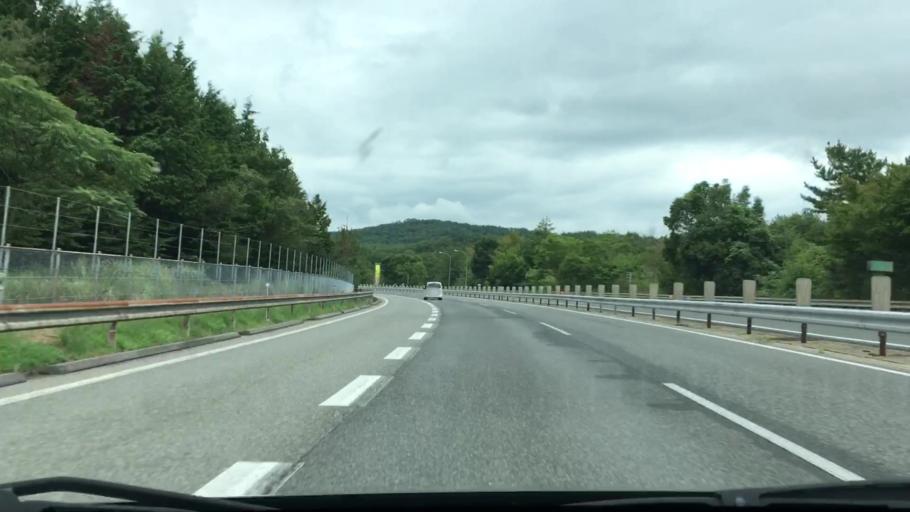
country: JP
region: Hiroshima
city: Miyoshi
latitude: 34.7565
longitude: 132.7569
